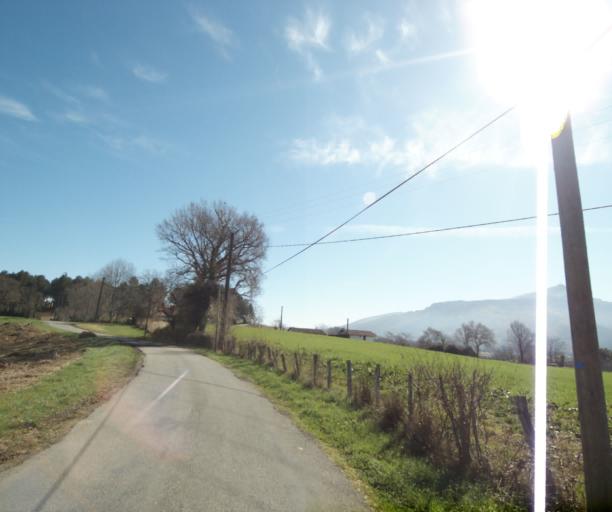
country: FR
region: Aquitaine
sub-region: Departement des Pyrenees-Atlantiques
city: Ciboure
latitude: 43.3512
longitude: -1.6652
